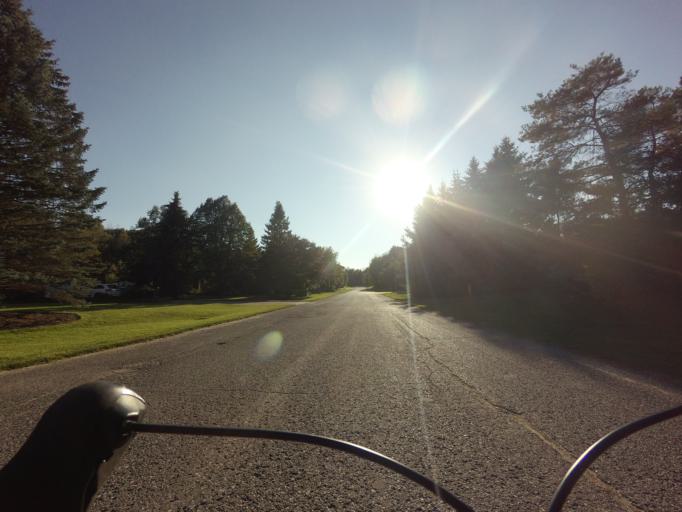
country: CA
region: Ontario
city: Bells Corners
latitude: 45.2155
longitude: -75.6933
